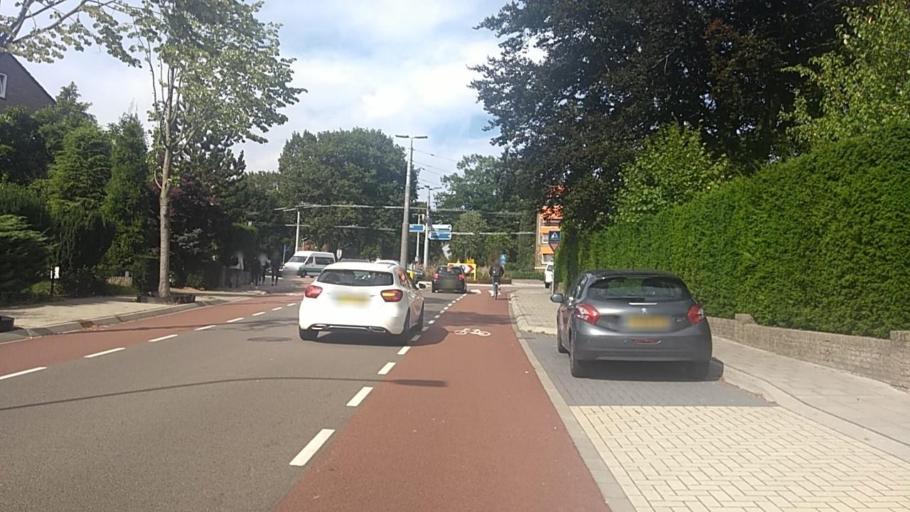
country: NL
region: Gelderland
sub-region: Gemeente Rozendaal
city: Rozendaal
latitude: 51.9955
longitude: 5.9633
